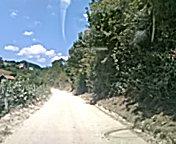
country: BA
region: Federation of Bosnia and Herzegovina
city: Orasac
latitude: 44.6217
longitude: 16.0602
